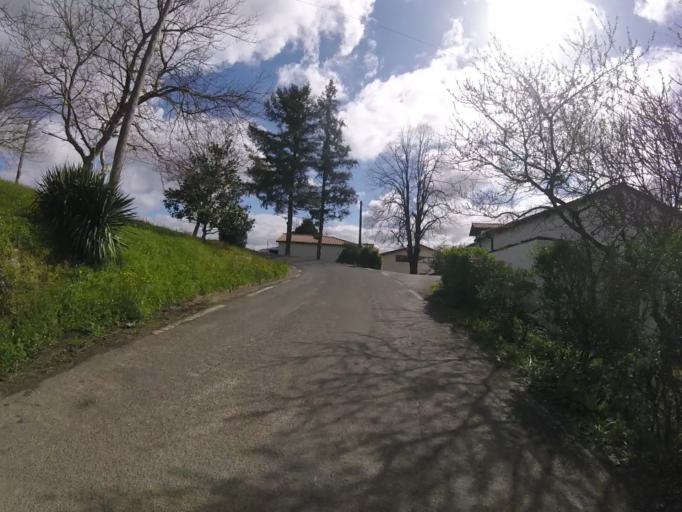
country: ES
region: Basque Country
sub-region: Provincia de Guipuzcoa
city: Tolosa
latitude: 43.1276
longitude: -2.0972
